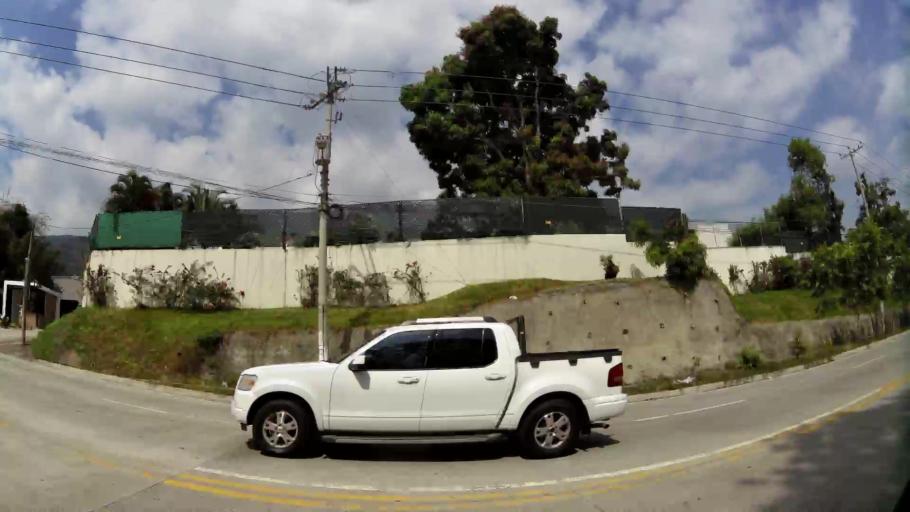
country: SV
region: San Salvador
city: Mejicanos
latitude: 13.7144
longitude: -89.2414
